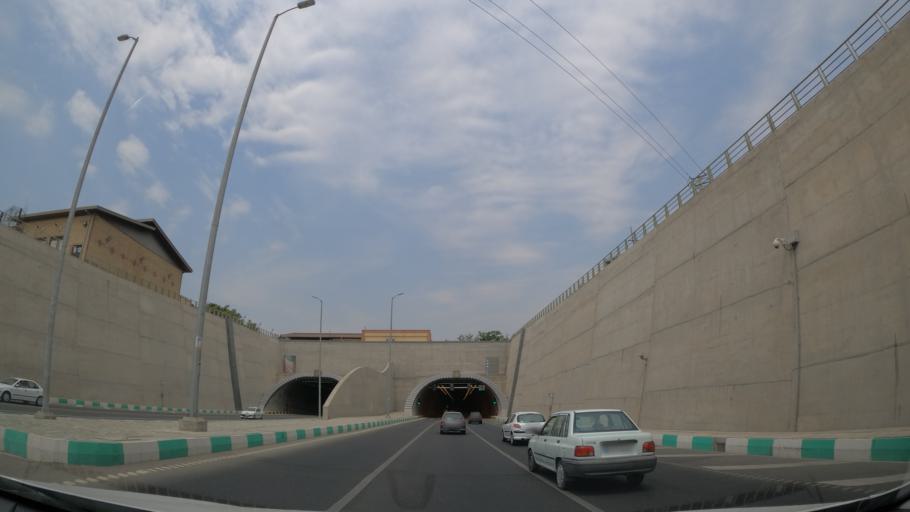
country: IR
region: Tehran
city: Shahr-e Qods
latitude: 35.7405
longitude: 51.2097
